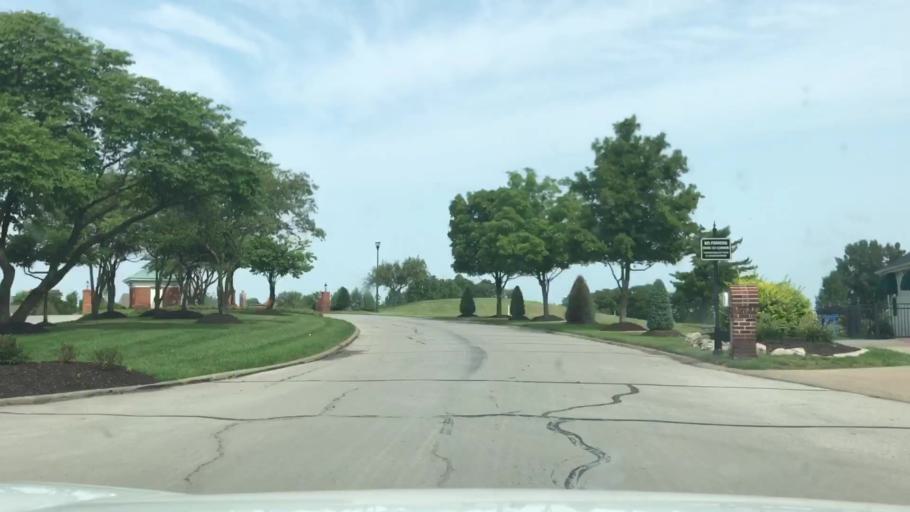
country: US
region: Missouri
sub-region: Saint Charles County
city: Cottleville
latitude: 38.7145
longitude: -90.6410
